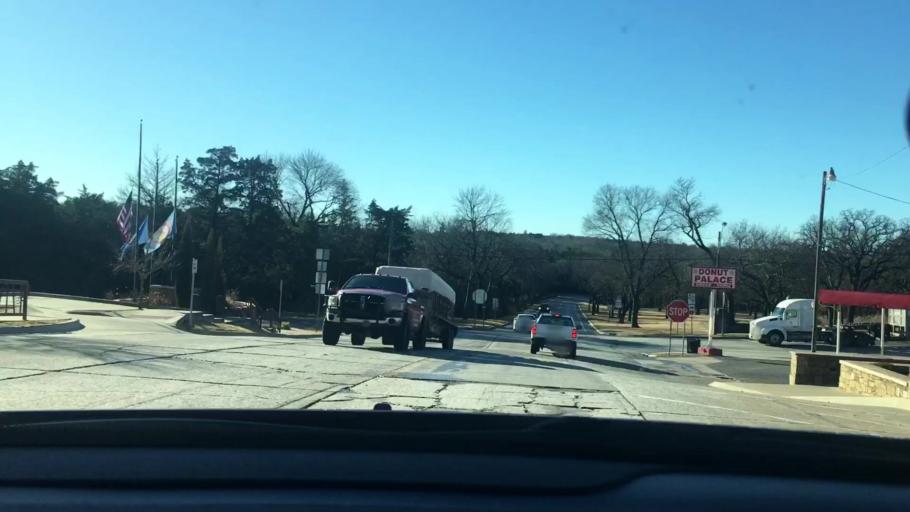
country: US
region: Oklahoma
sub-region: Murray County
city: Sulphur
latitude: 34.5069
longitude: -96.9688
